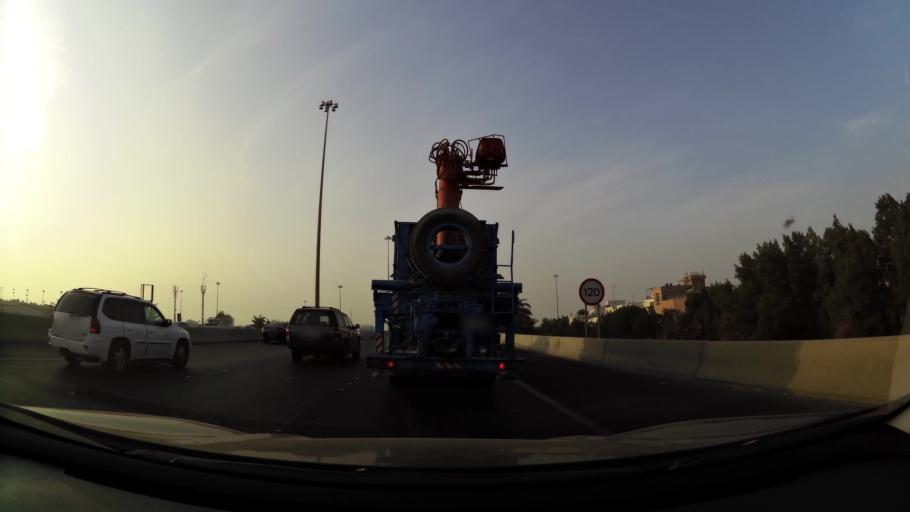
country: KW
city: Bayan
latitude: 29.3026
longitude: 48.0624
